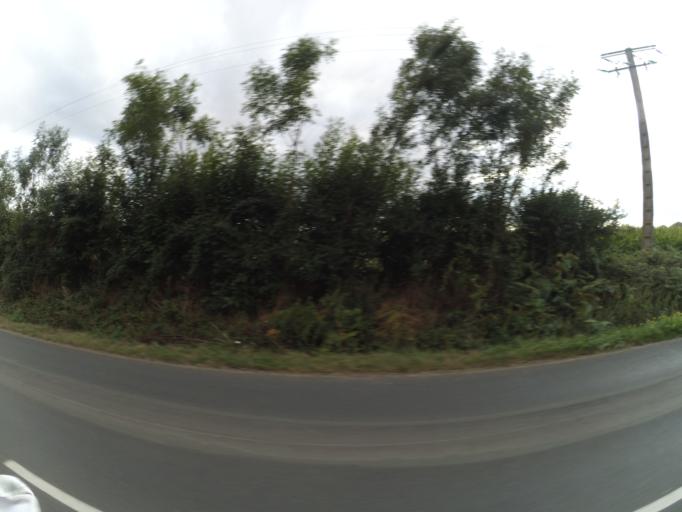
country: FR
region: Pays de la Loire
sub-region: Departement de la Vendee
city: Saint-Andre-Treize-Voies
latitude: 46.9288
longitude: -1.4008
